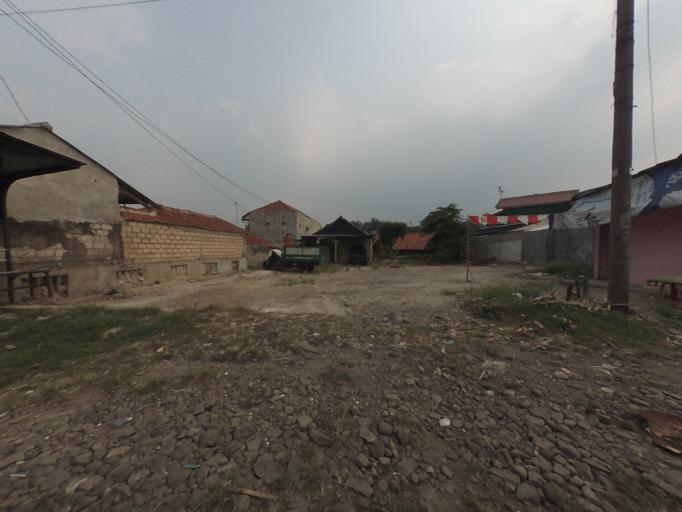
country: ID
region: West Java
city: Ciampea
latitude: -6.5596
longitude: 106.6904
